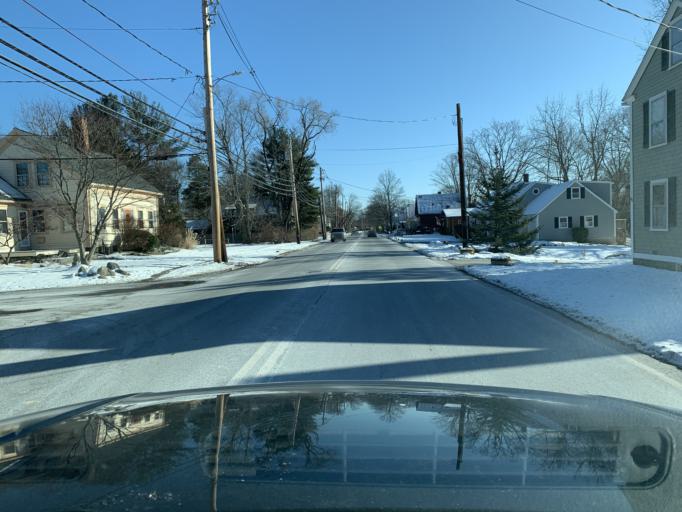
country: US
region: Massachusetts
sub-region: Essex County
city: Danvers
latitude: 42.5669
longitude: -70.9648
